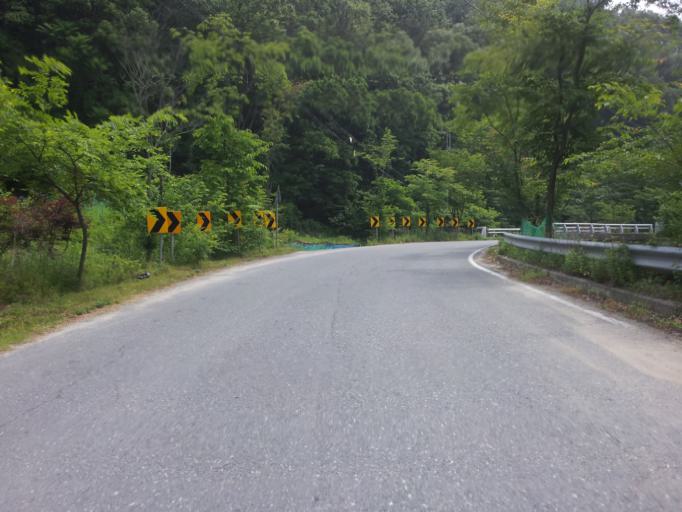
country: KR
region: Daejeon
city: Daejeon
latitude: 36.3326
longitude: 127.4896
